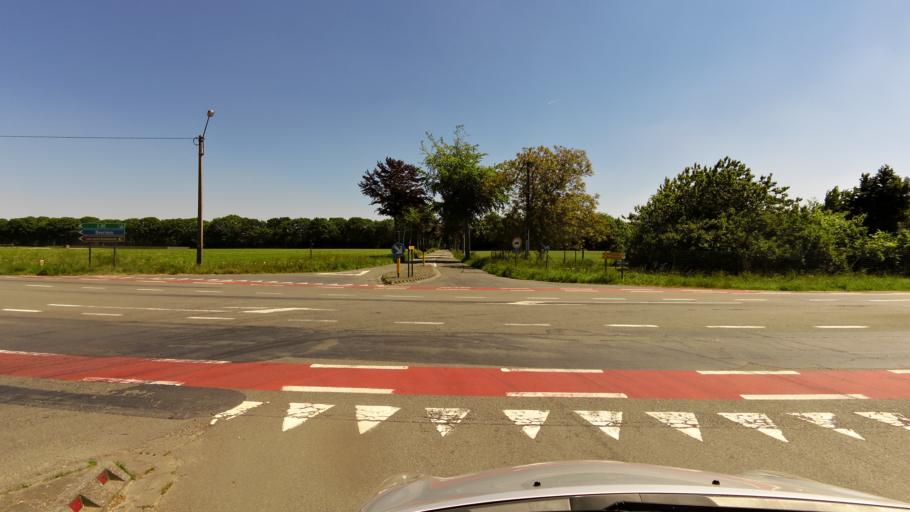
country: BE
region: Flanders
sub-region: Provincie West-Vlaanderen
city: Oostkamp
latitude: 51.1162
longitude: 3.2739
